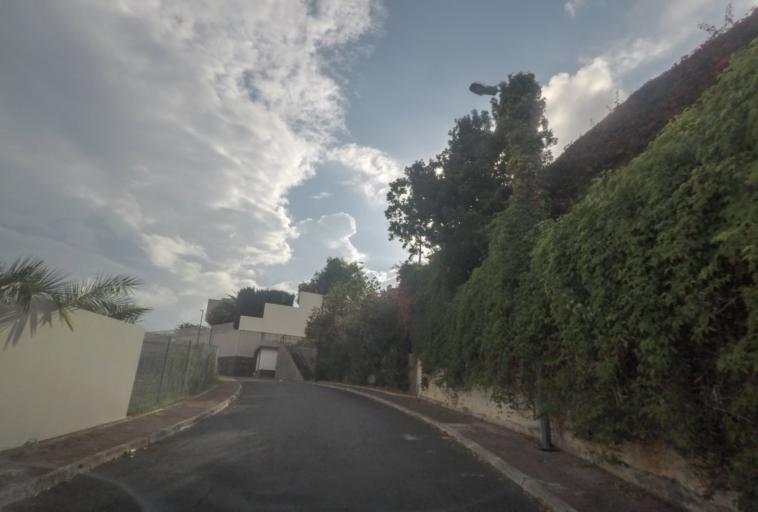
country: PT
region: Madeira
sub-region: Funchal
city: Funchal
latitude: 32.6425
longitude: -16.9315
